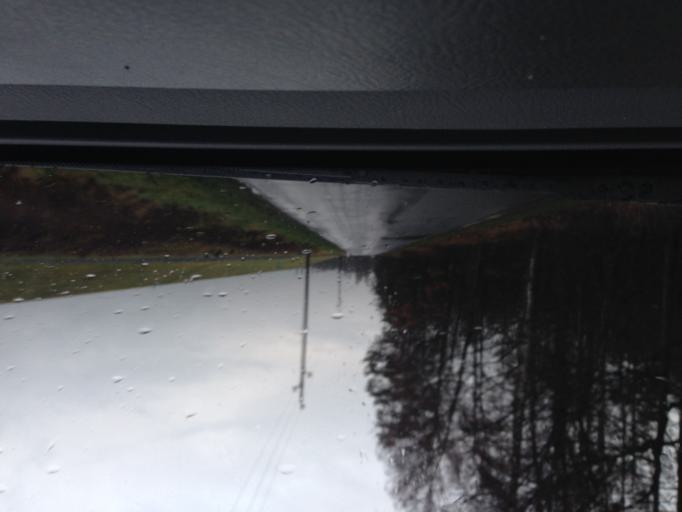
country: PL
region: Opole Voivodeship
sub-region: Powiat opolski
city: Chrzastowice
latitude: 50.7138
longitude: 18.0882
